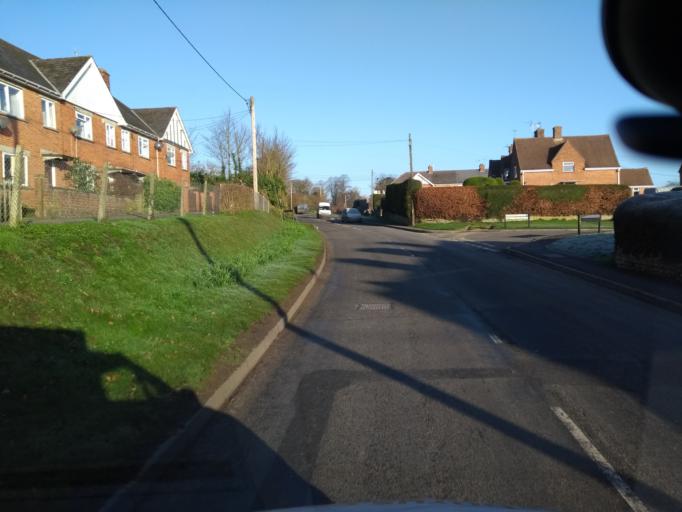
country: GB
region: England
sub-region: Somerset
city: Bruton
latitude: 51.1158
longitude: -2.4486
